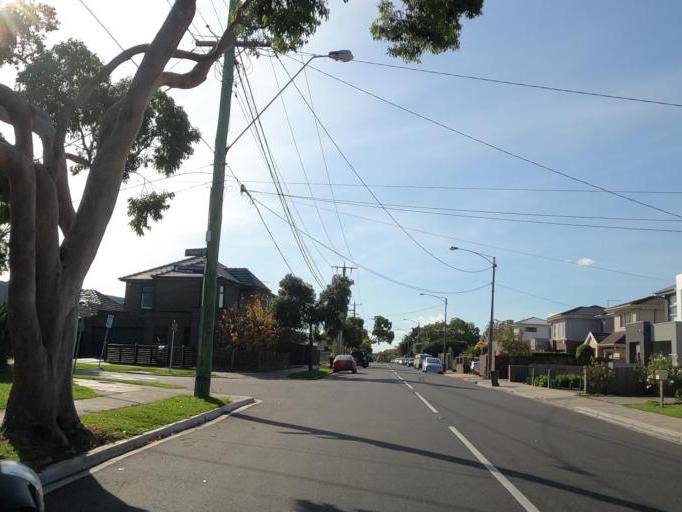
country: AU
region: Victoria
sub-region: Moonee Valley
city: Airport West
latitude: -37.7312
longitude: 144.8808
